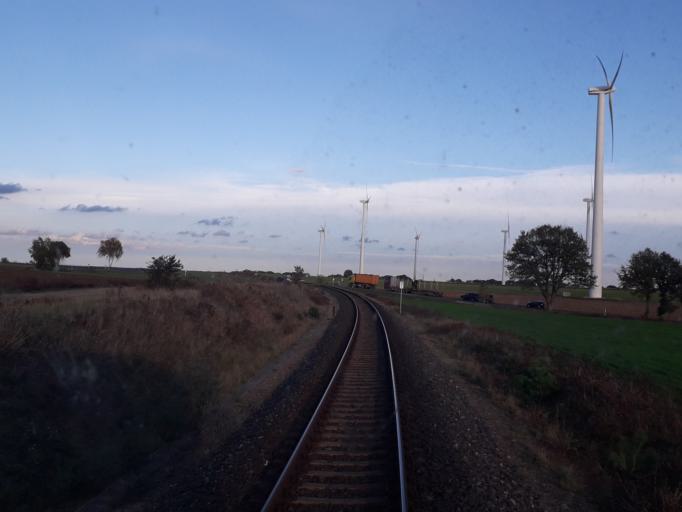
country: DE
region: Brandenburg
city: Heiligengrabe
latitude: 53.1548
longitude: 12.4162
